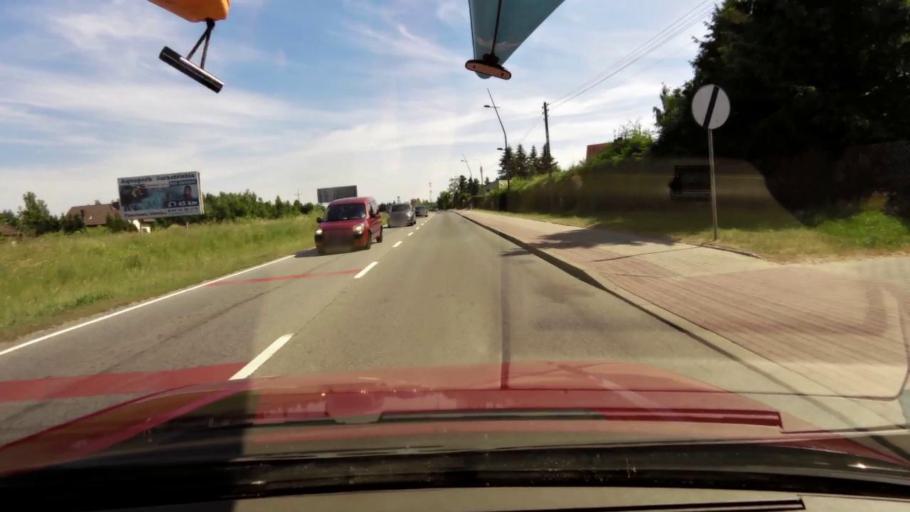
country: PL
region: Pomeranian Voivodeship
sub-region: Powiat slupski
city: Kobylnica
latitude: 54.4366
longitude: 16.9981
